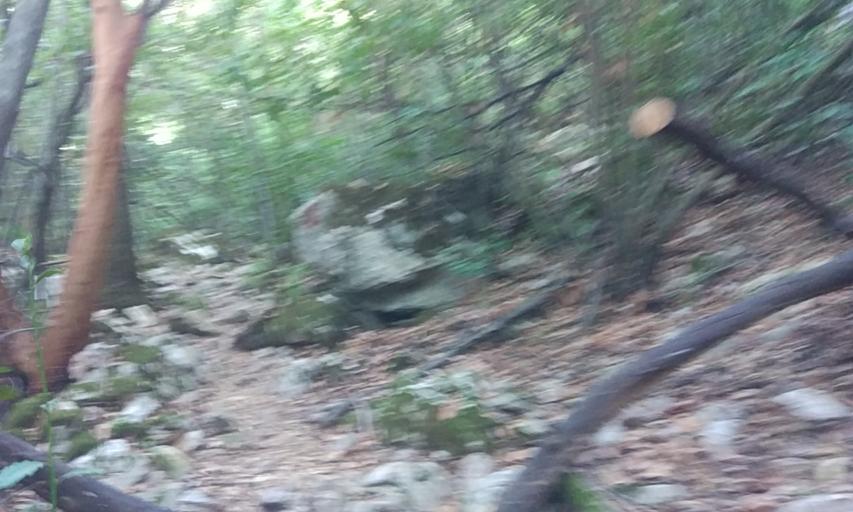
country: TR
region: Antalya
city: Tekirova
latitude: 36.3777
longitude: 30.4790
